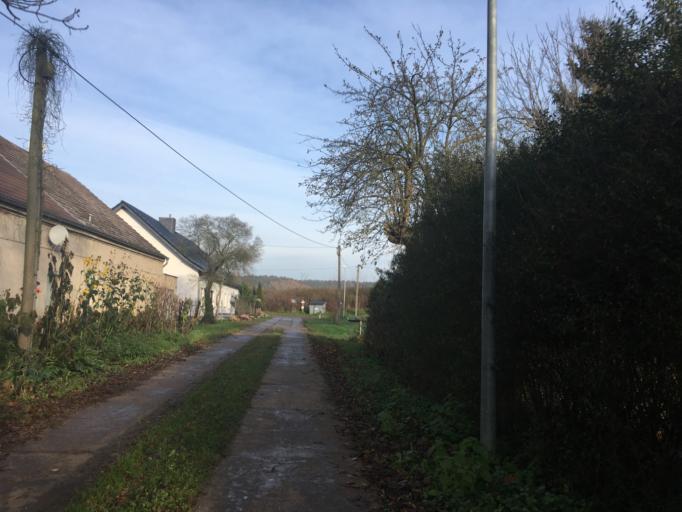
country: DE
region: Brandenburg
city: Bad Freienwalde
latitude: 52.8087
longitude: 14.0132
